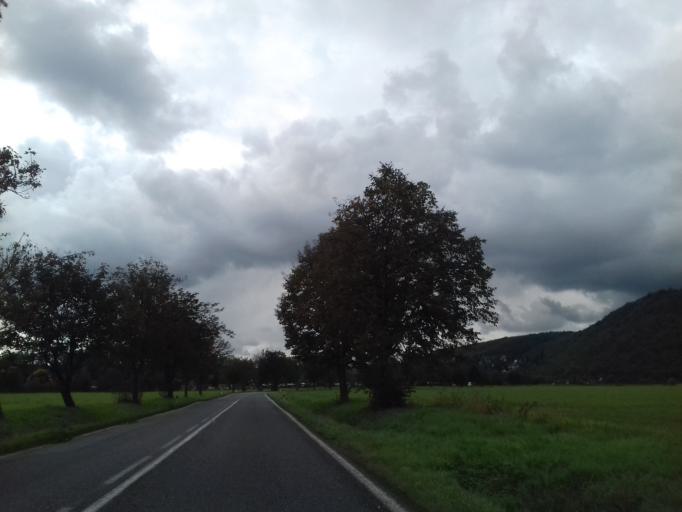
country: CZ
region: Central Bohemia
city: Cernosice
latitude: 49.9717
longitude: 14.3426
